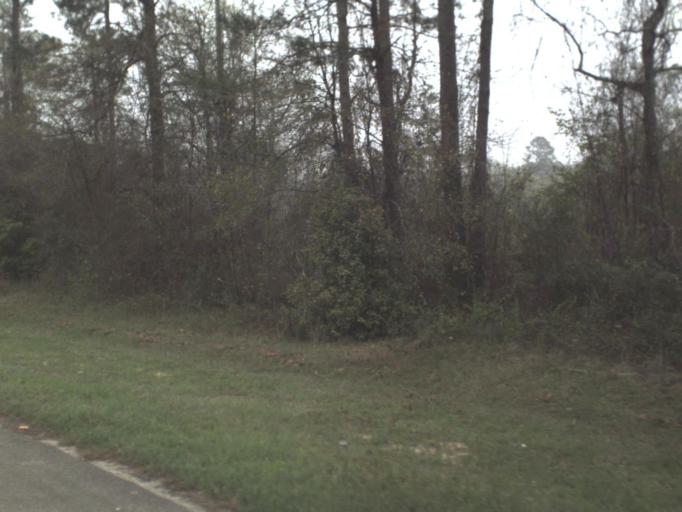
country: US
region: Florida
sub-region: Gadsden County
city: Gretna
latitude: 30.5107
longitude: -84.7083
